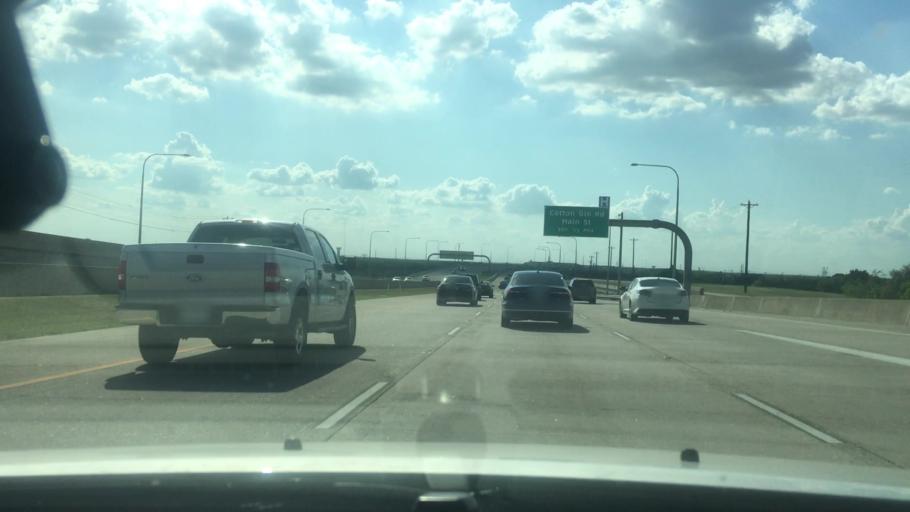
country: US
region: Texas
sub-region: Collin County
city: Frisco
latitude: 33.1352
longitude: -96.8297
